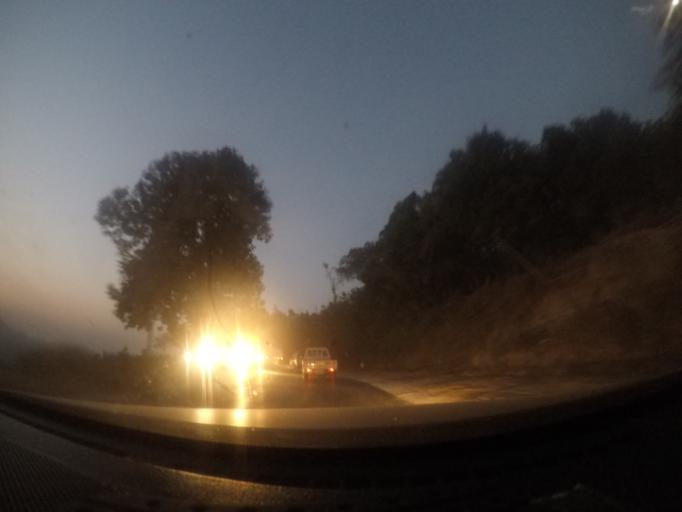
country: MM
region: Mandalay
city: Yamethin
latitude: 20.7053
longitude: 96.5159
